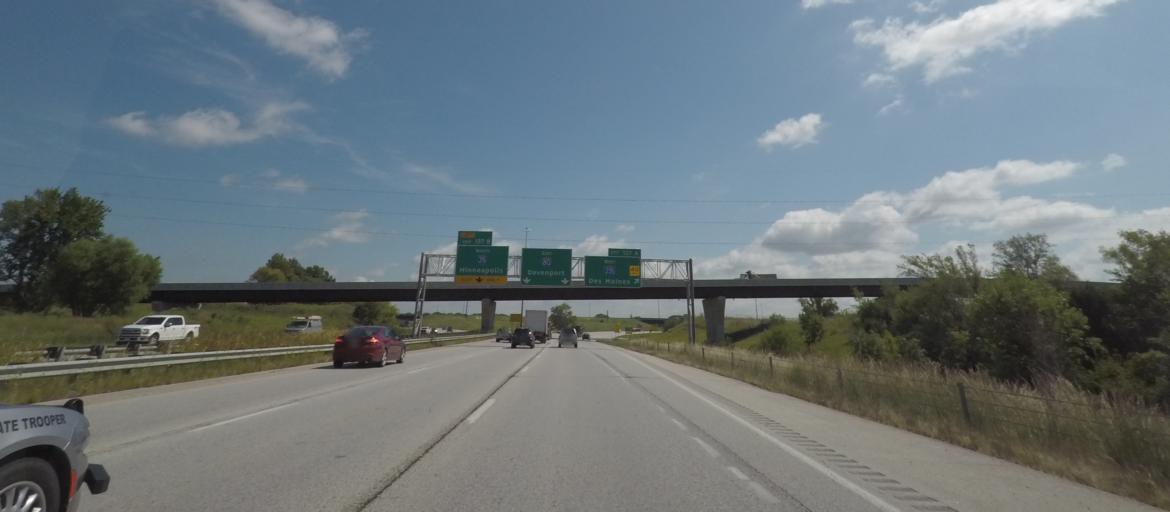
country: US
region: Iowa
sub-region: Polk County
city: Saylorville
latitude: 41.6506
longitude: -93.5814
